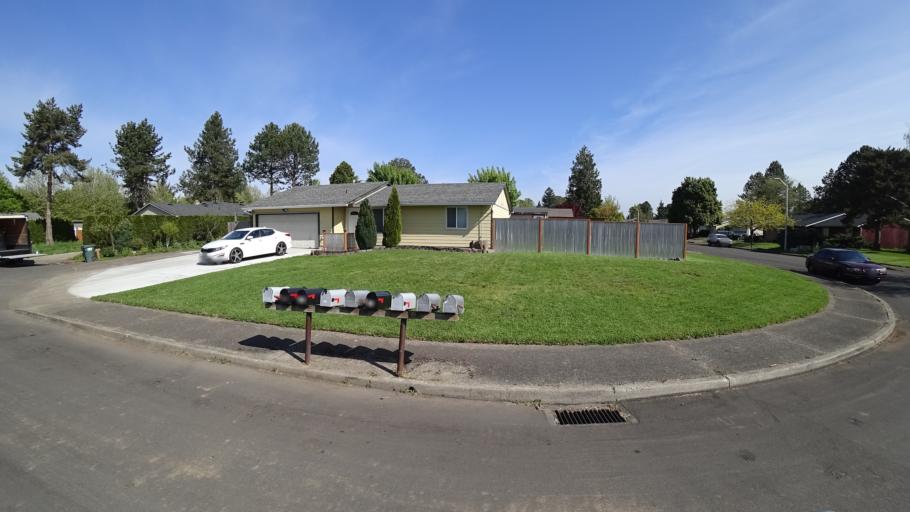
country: US
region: Oregon
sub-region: Washington County
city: Hillsboro
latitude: 45.5232
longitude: -122.9483
